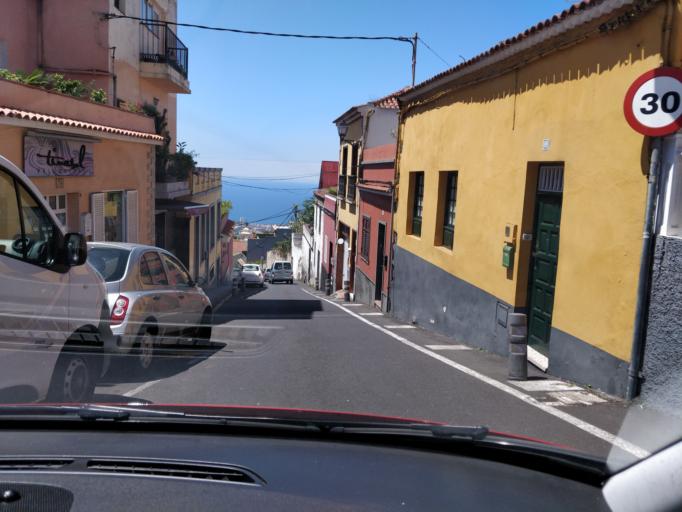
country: ES
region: Canary Islands
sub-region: Provincia de Santa Cruz de Tenerife
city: La Orotava
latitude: 28.3850
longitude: -16.5219
